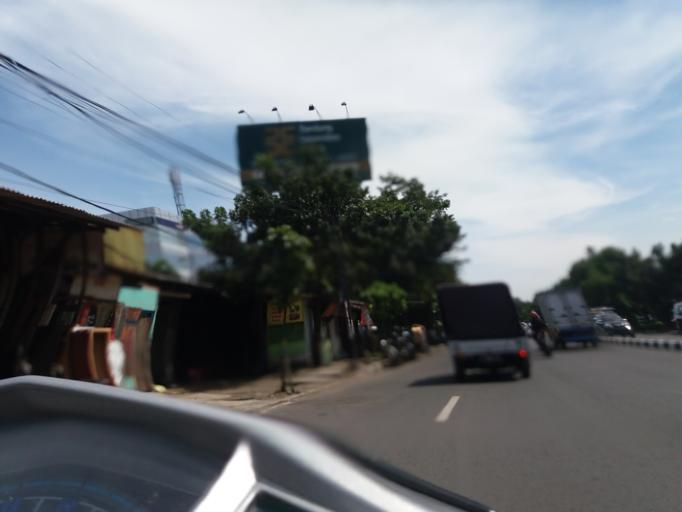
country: ID
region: West Java
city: Margahayukencana
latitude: -6.9477
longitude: 107.5986
